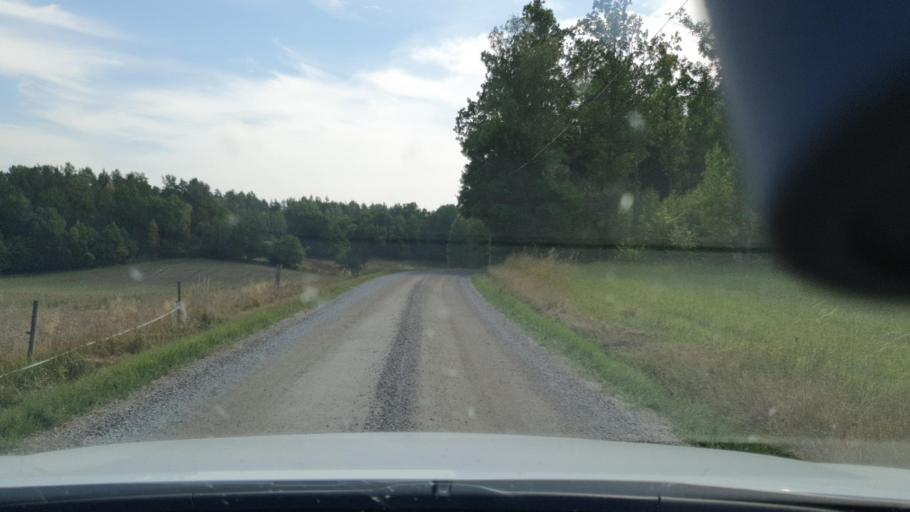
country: SE
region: Kalmar
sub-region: Vasterviks Kommun
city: Ankarsrum
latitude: 57.7029
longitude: 16.4542
